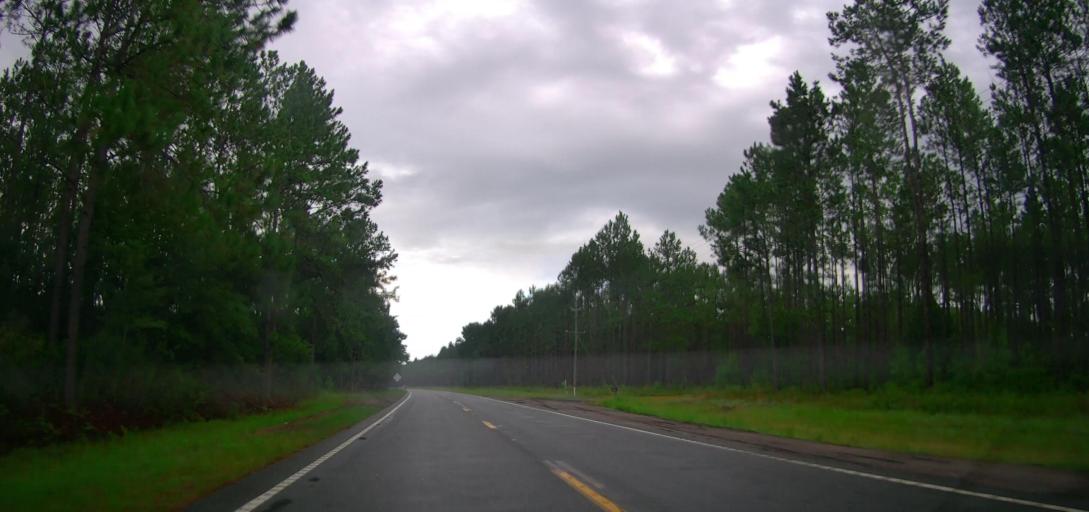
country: US
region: Georgia
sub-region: Ware County
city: Deenwood
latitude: 31.2659
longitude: -82.5200
